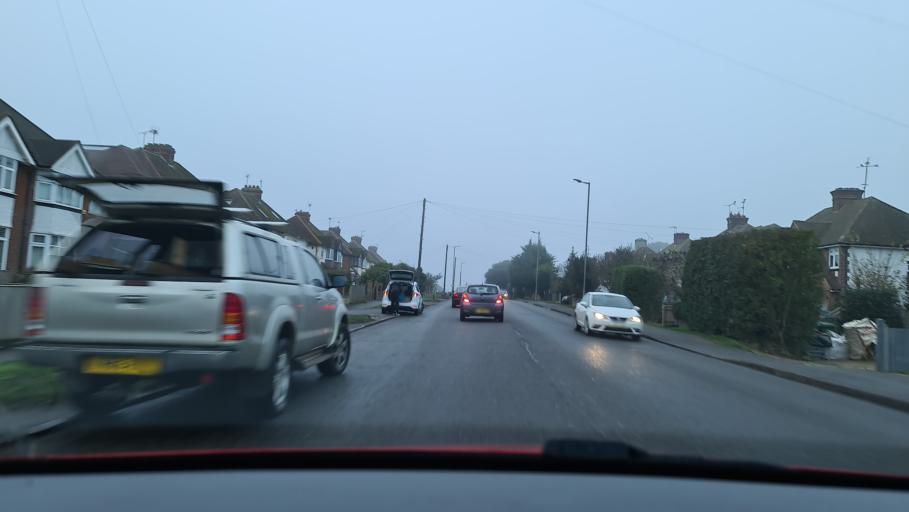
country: GB
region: England
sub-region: Buckinghamshire
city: Weston Turville
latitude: 51.8126
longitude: -0.7804
